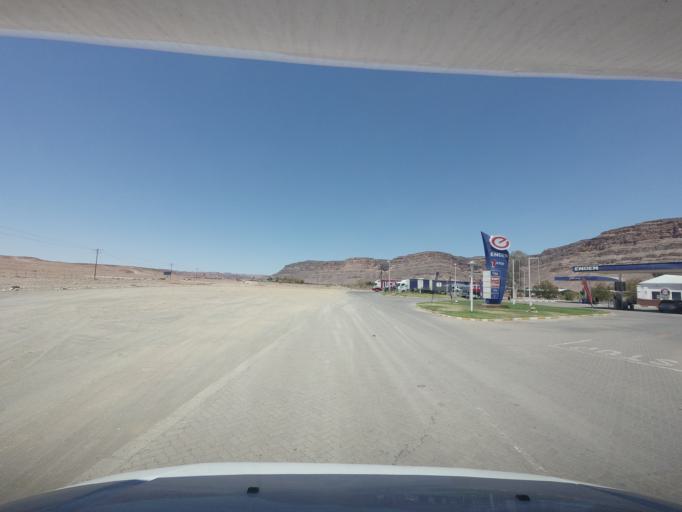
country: ZA
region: Northern Cape
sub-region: Namakwa District Municipality
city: Port Nolloth
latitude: -28.7367
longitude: 17.6163
